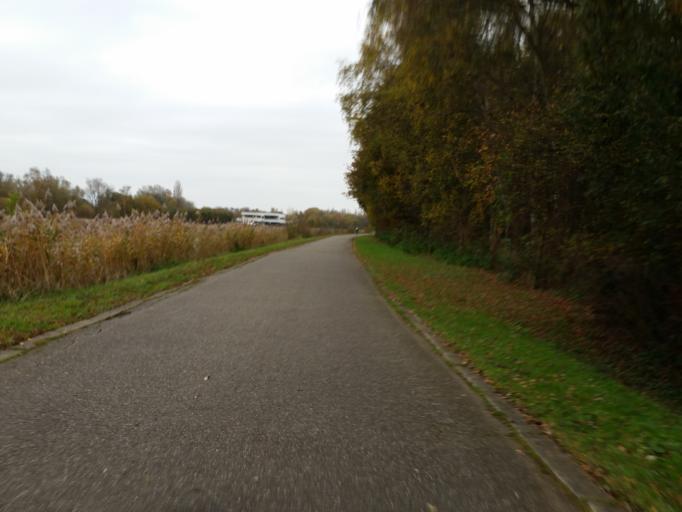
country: BE
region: Flanders
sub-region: Provincie Antwerpen
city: Duffel
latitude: 51.1057
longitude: 4.5226
